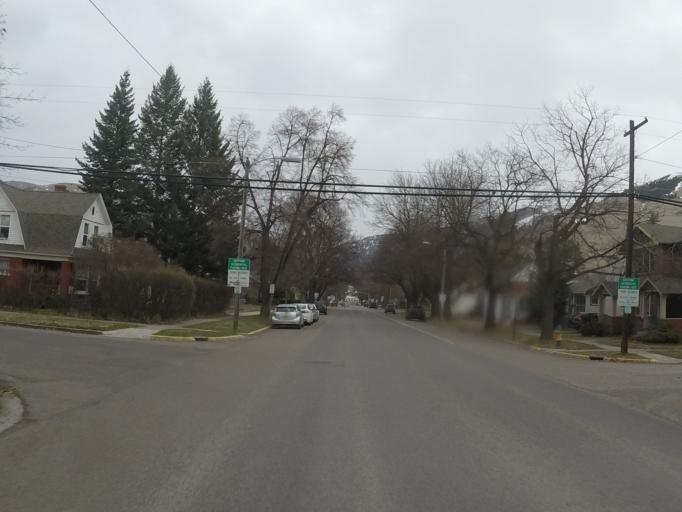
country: US
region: Montana
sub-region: Missoula County
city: Missoula
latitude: 46.8640
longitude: -113.9928
